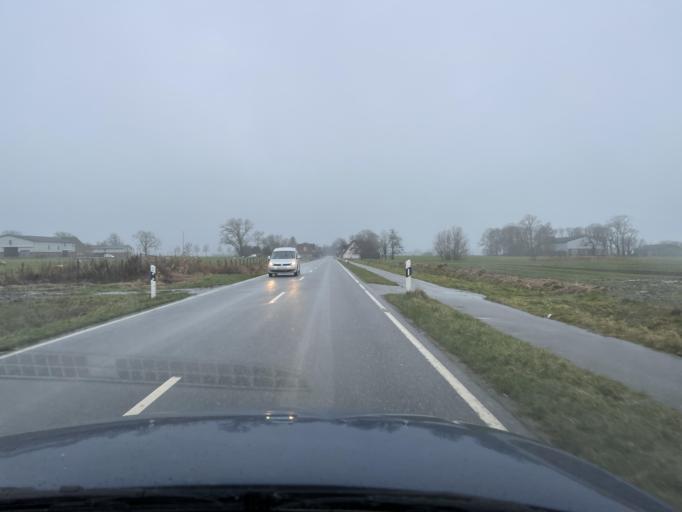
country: DE
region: Schleswig-Holstein
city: Neuenkirchen
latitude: 54.2394
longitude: 9.0123
